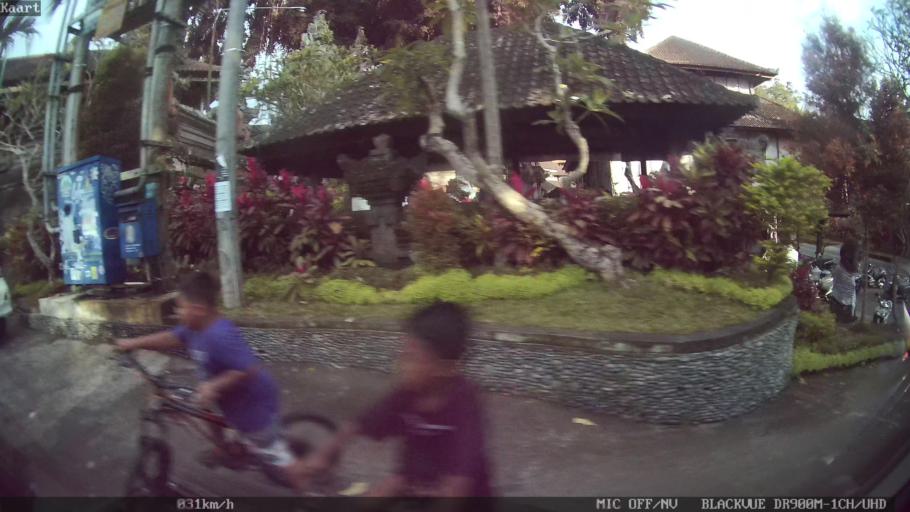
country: ID
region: Bali
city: Banjar Pande
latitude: -8.5097
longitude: 115.2484
